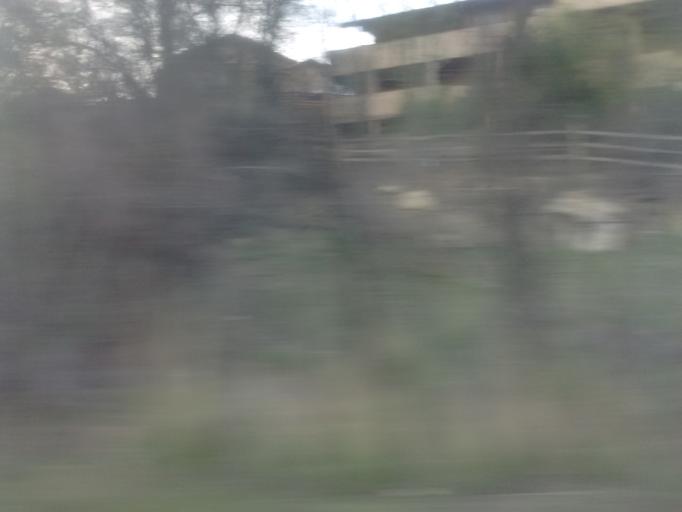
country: US
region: Colorado
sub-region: Mesa County
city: Redlands
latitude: 39.0837
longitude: -108.6297
